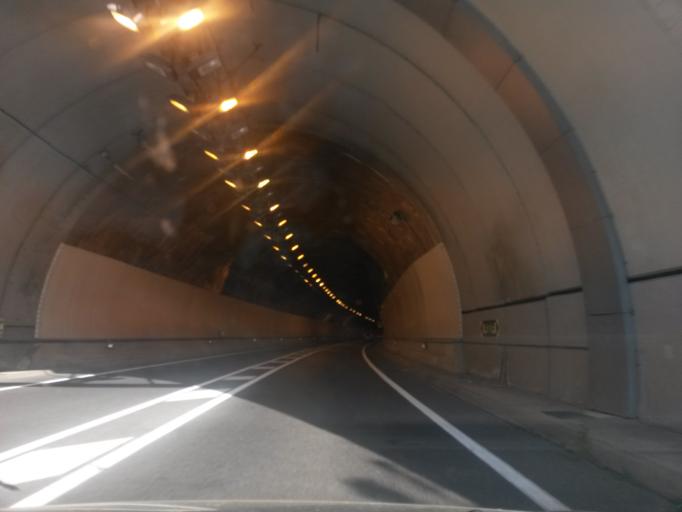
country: ES
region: Catalonia
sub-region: Provincia de Girona
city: Bas
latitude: 42.1211
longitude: 2.4656
